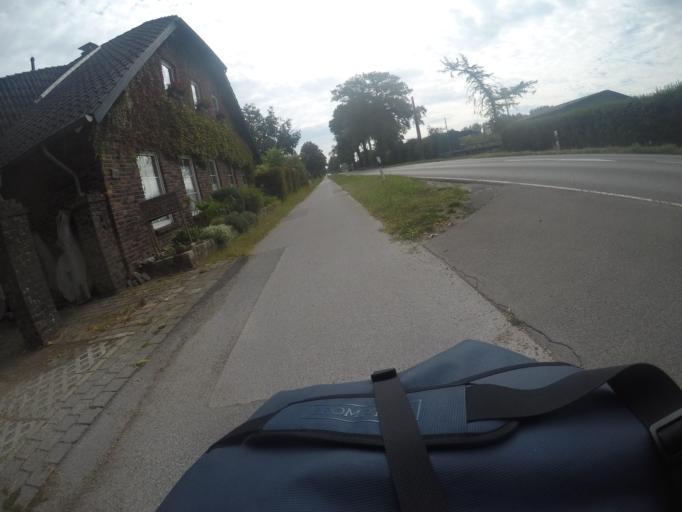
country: DE
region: North Rhine-Westphalia
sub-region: Regierungsbezirk Dusseldorf
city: Emmerich
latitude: 51.8434
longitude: 6.2153
